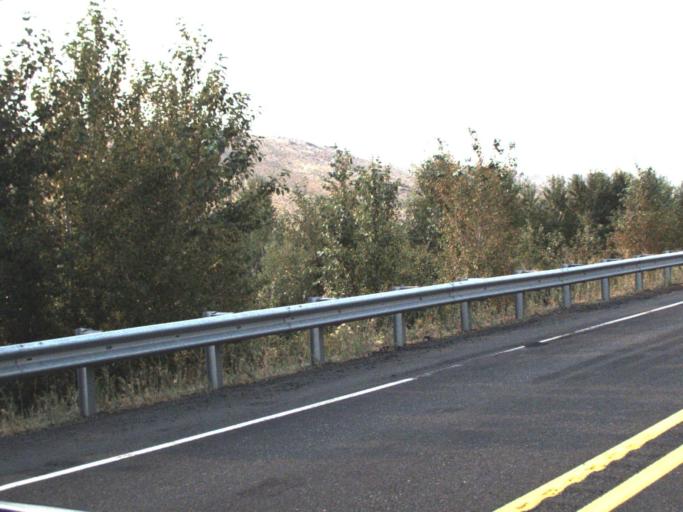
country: US
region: Washington
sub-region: Yakima County
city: Toppenish
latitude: 46.1955
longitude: -120.4889
